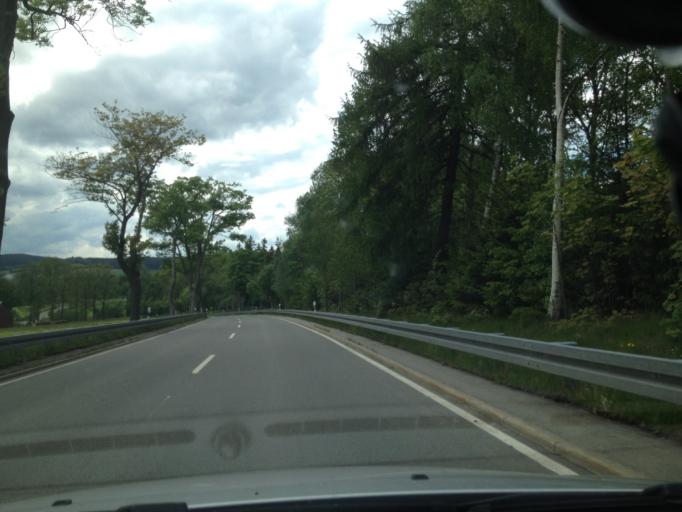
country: DE
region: Saxony
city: Barenstein
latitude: 50.5208
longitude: 13.0148
